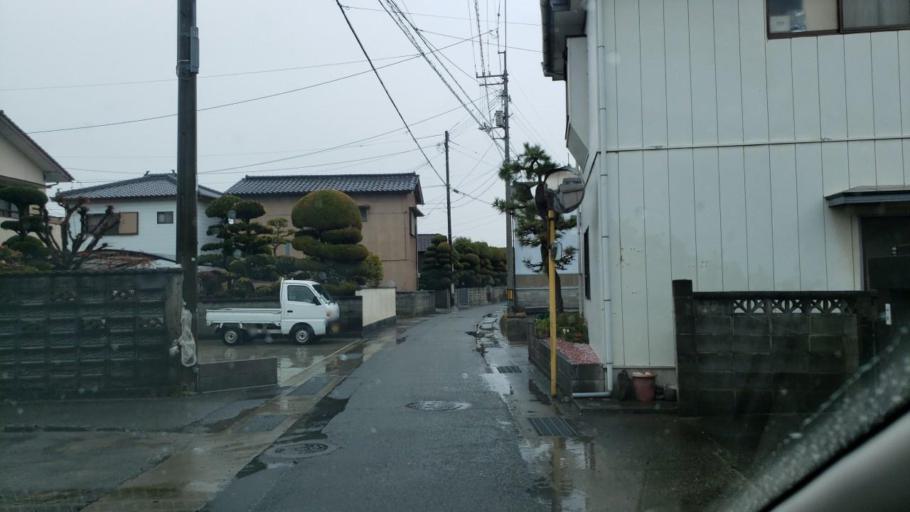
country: JP
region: Tokushima
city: Kamojimacho-jogejima
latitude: 34.0763
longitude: 134.3485
